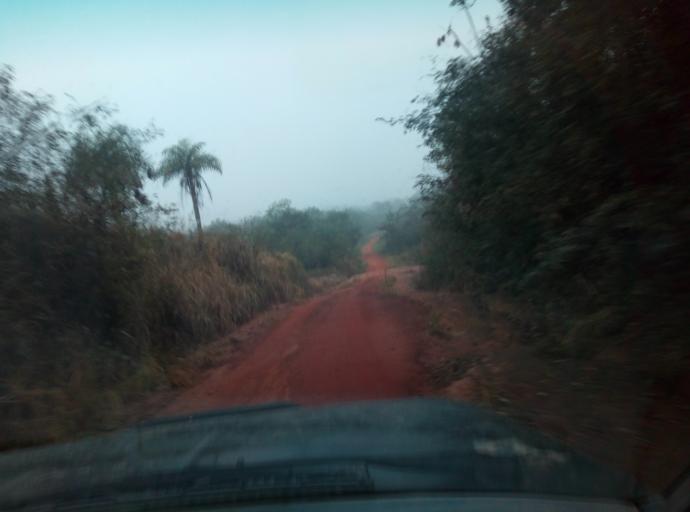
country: PY
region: Caaguazu
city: Doctor Cecilio Baez
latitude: -25.1587
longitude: -56.2558
